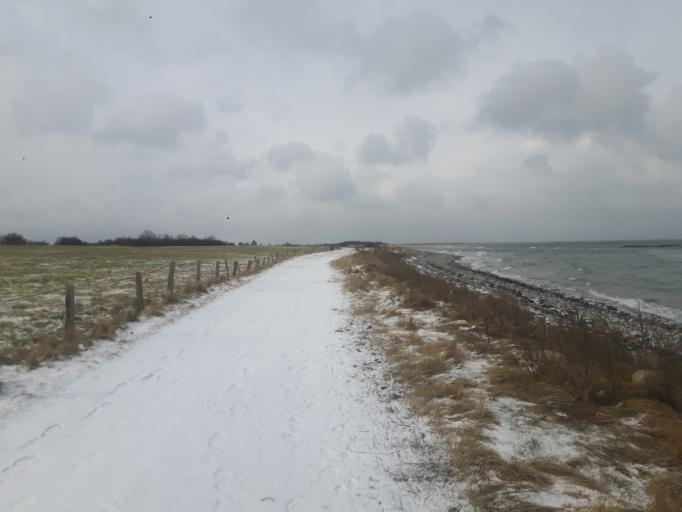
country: DE
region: Schleswig-Holstein
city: Fehmarn
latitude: 54.5066
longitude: 11.2074
